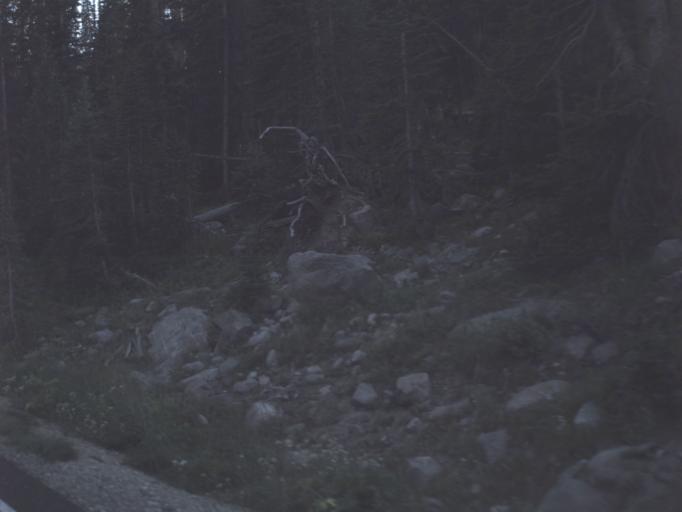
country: US
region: Utah
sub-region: Summit County
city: Kamas
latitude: 40.7539
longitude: -110.8783
